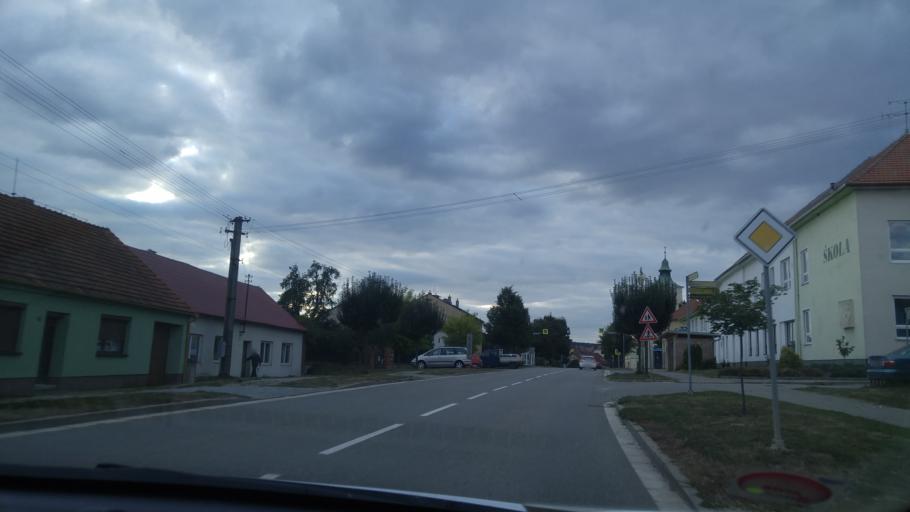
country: CZ
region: South Moravian
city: Ricany
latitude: 49.2102
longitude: 16.4106
